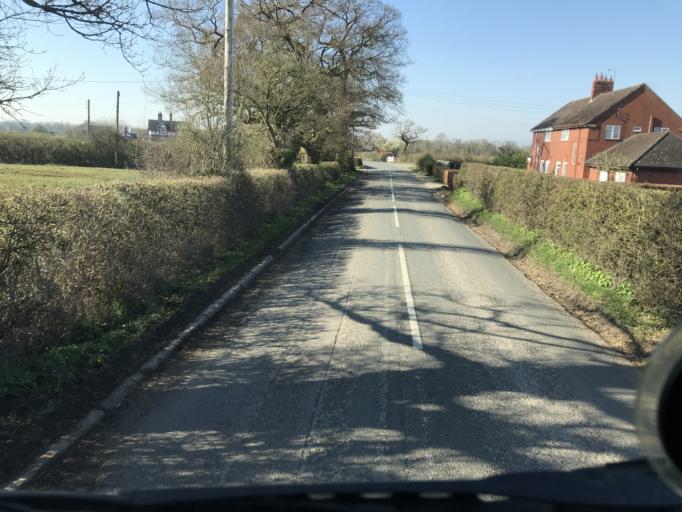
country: GB
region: England
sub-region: Cheshire West and Chester
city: Aldford
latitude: 53.1361
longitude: -2.8448
